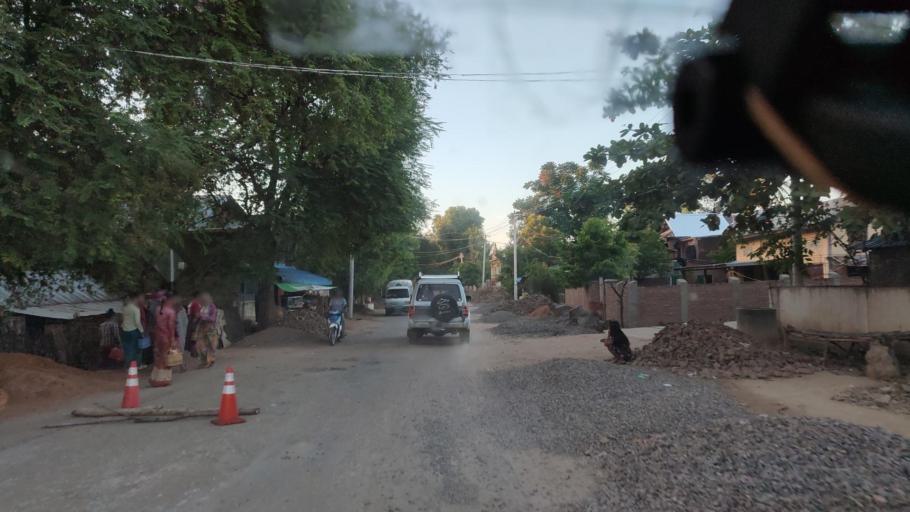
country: MM
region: Magway
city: Magway
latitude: 20.0987
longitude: 94.9133
